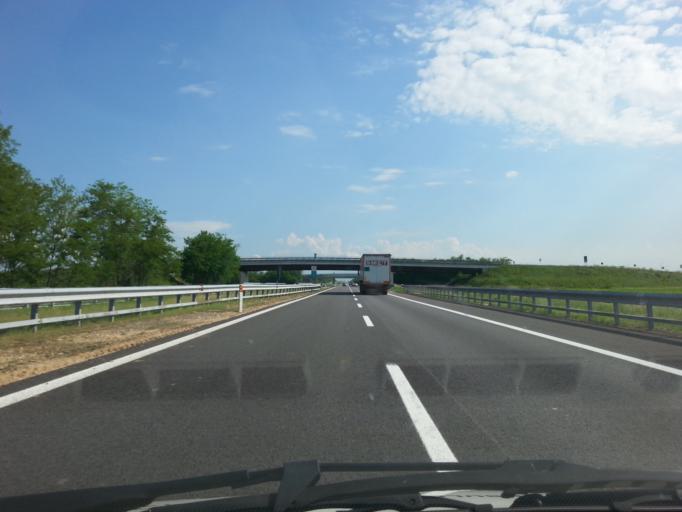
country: IT
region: Piedmont
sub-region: Provincia di Cuneo
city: Caramagna Piemonte
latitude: 44.8190
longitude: 7.7510
